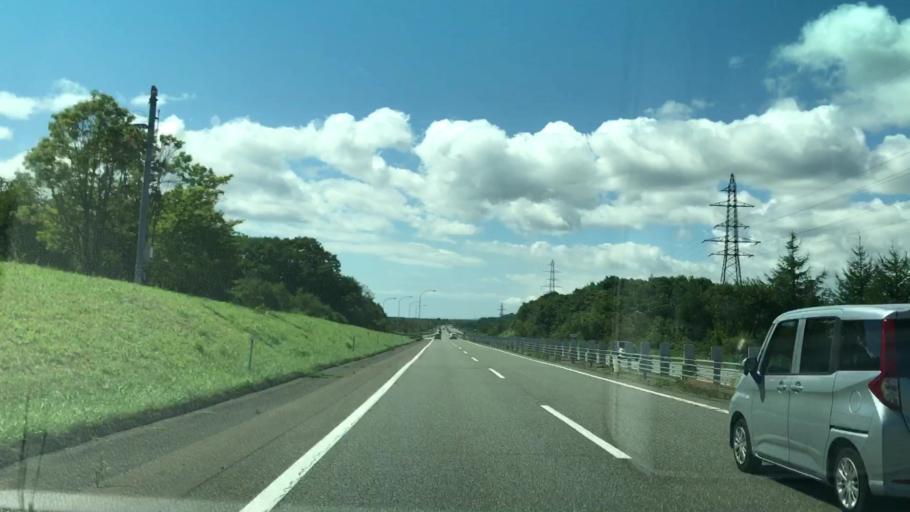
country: JP
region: Hokkaido
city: Shiraoi
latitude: 42.6105
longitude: 141.4625
